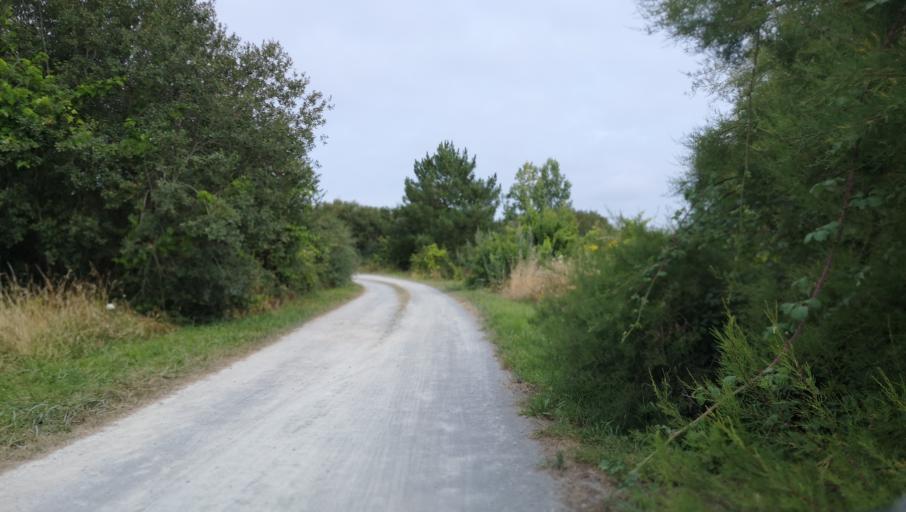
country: FR
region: Pays de la Loire
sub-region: Departement de la Vendee
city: Olonne-sur-Mer
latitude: 46.5292
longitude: -1.8021
